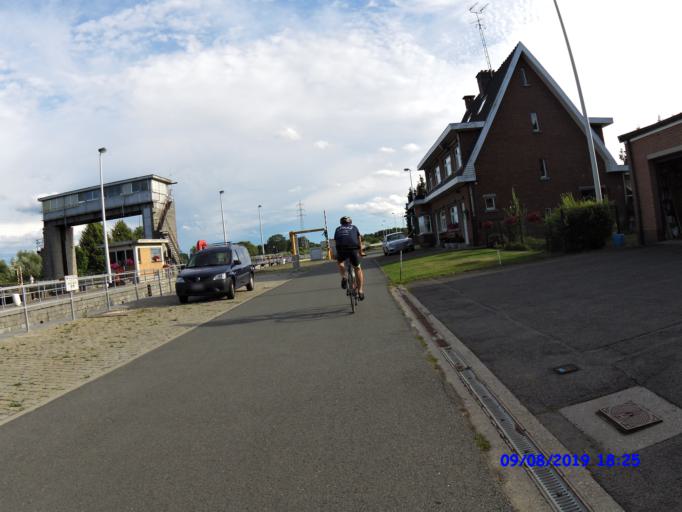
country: BE
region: Flanders
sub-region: Provincie Oost-Vlaanderen
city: Dendermonde
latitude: 51.0011
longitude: 4.0777
